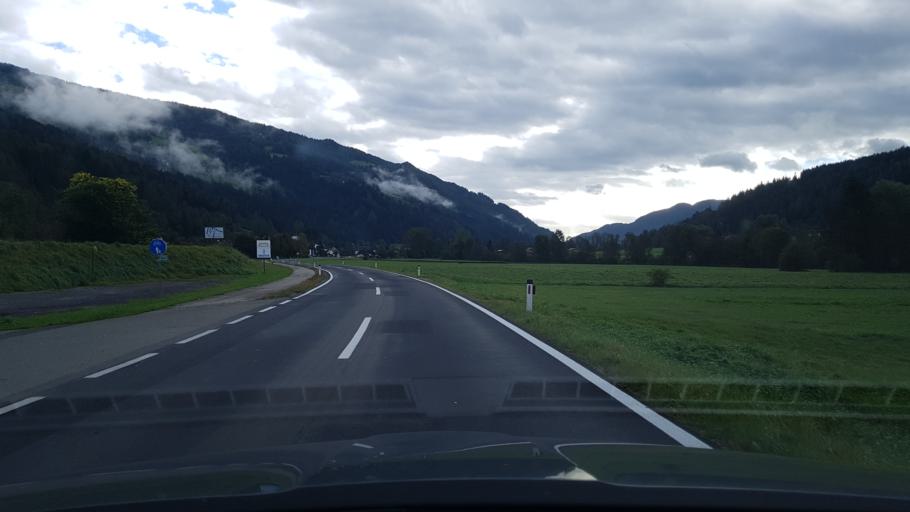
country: AT
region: Styria
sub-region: Politischer Bezirk Murau
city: Winklern bei Oberwolz
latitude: 47.1795
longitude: 14.2150
